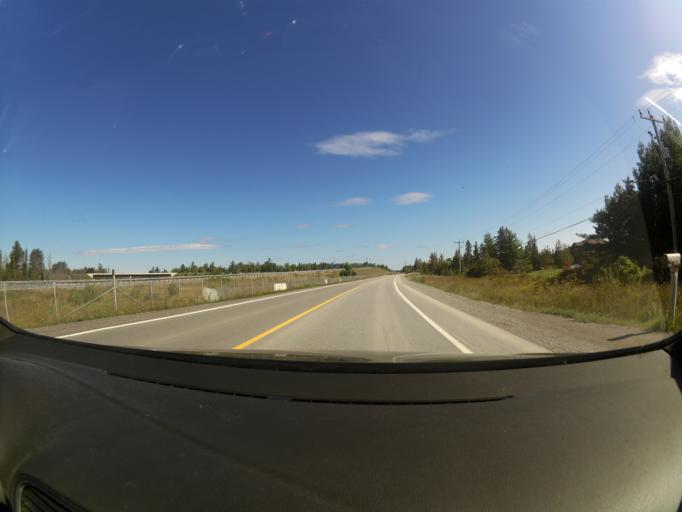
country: CA
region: Ontario
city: Bells Corners
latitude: 45.2463
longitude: -75.9706
